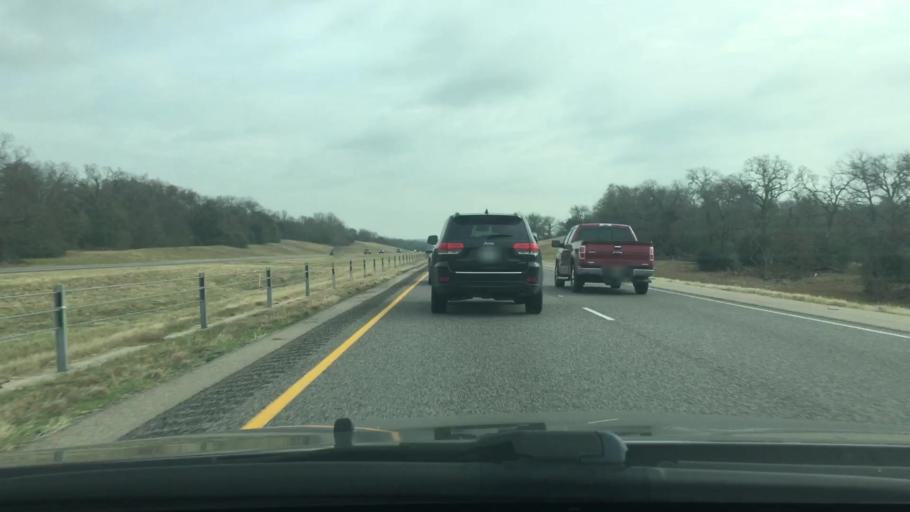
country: US
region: Texas
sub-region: Leon County
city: Buffalo
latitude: 31.5205
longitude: -96.1099
